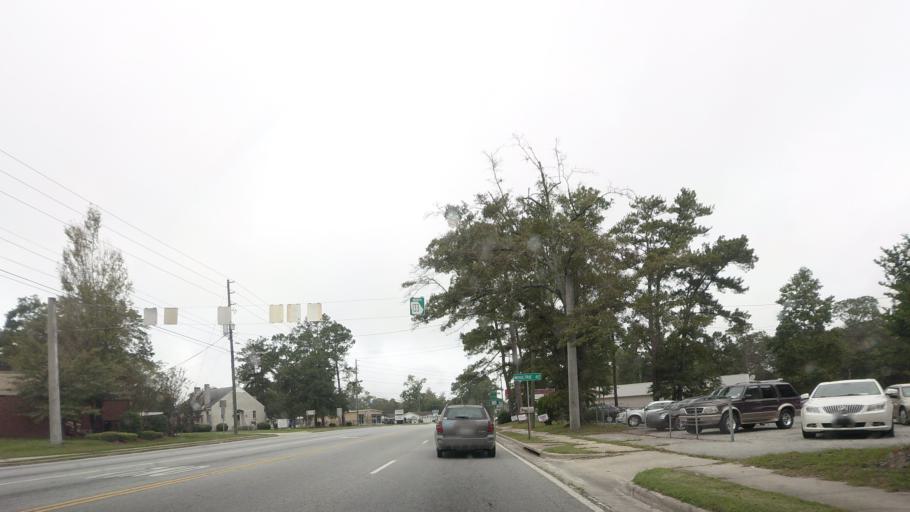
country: US
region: Georgia
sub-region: Lowndes County
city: Remerton
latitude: 30.8237
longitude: -83.3049
